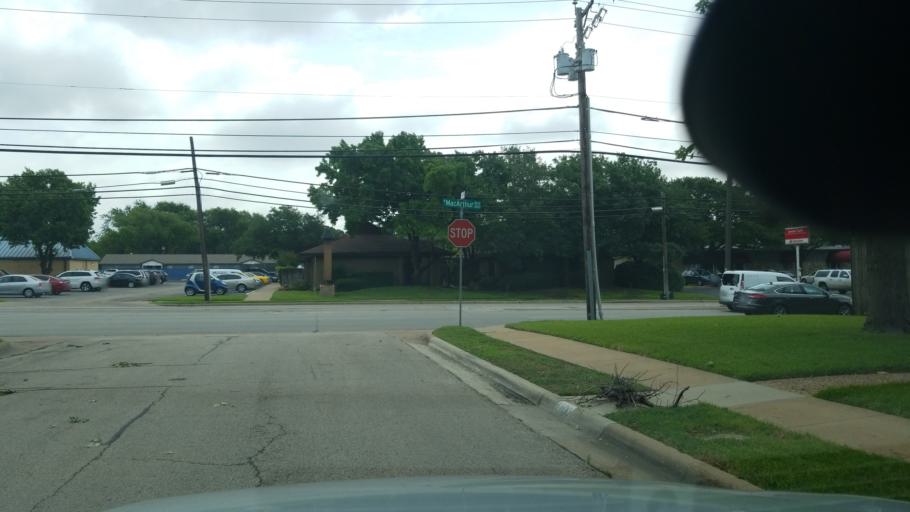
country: US
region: Texas
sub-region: Dallas County
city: Irving
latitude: 32.8473
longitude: -96.9594
